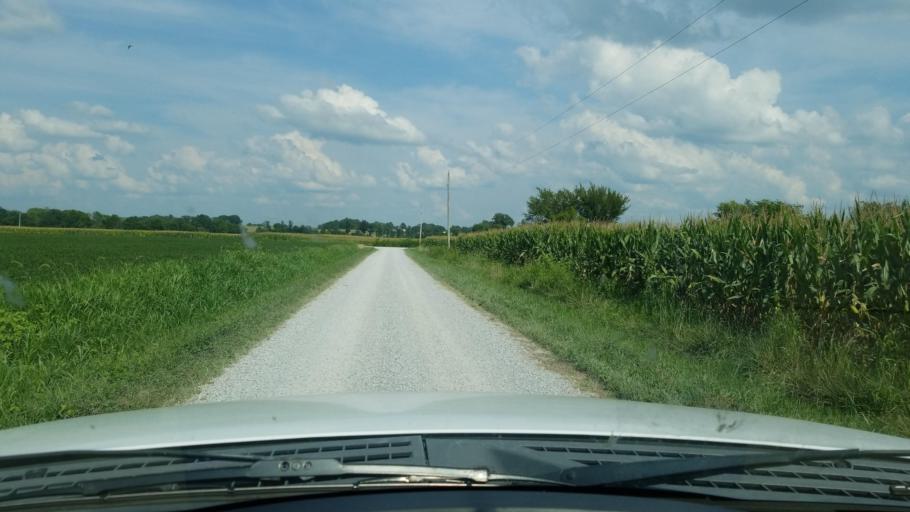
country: US
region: Illinois
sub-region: Saline County
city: Eldorado
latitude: 37.8468
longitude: -88.4821
